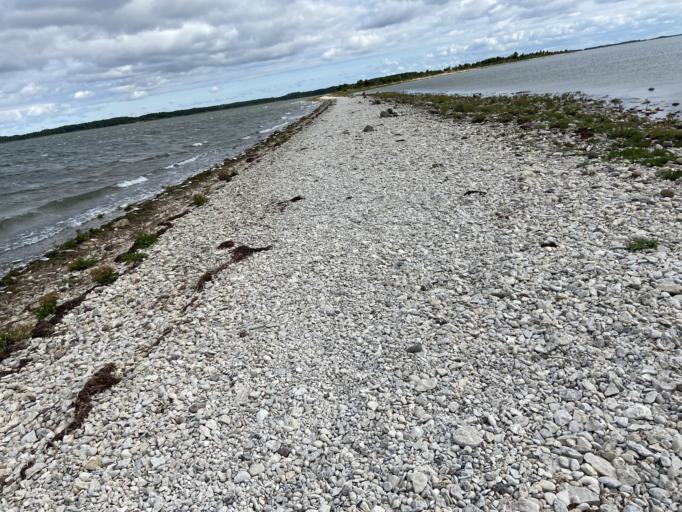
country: EE
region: Hiiumaa
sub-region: Kaerdla linn
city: Kardla
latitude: 58.7573
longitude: 22.7922
